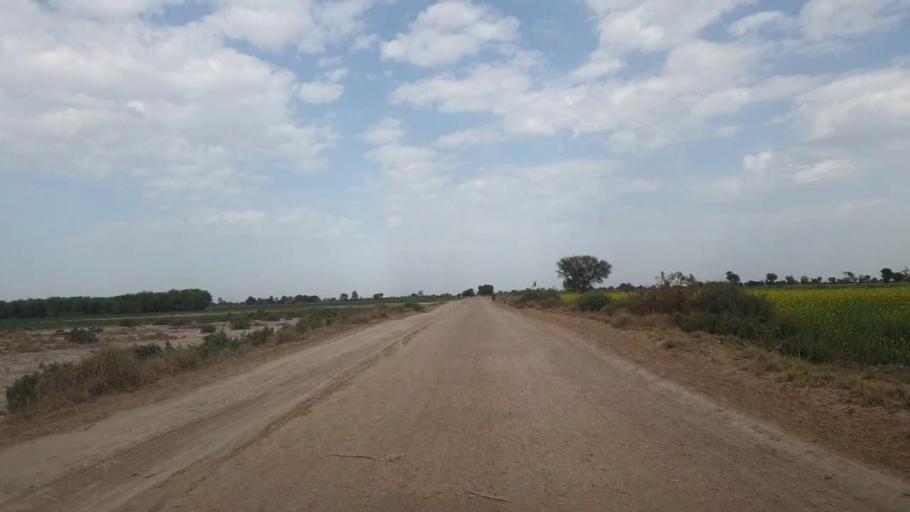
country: PK
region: Sindh
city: Hala
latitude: 25.9602
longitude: 68.4668
